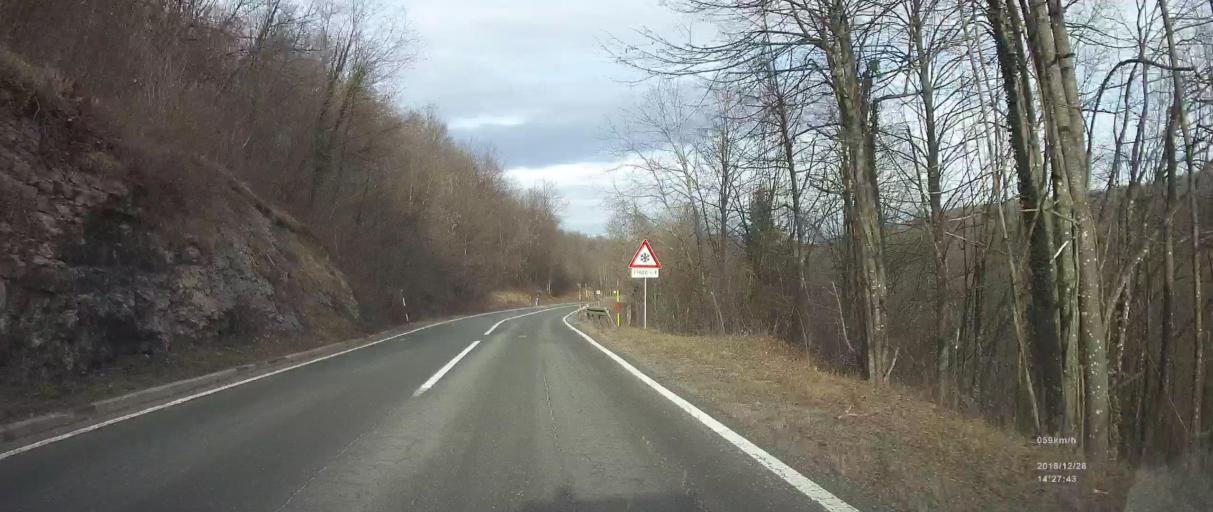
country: HR
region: Primorsko-Goranska
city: Vrbovsko
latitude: 45.4041
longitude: 15.1086
